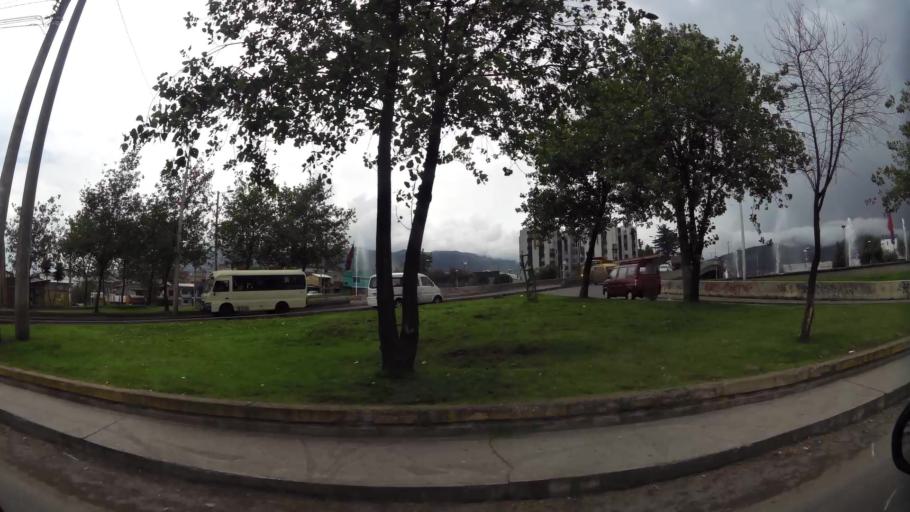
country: EC
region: Pichincha
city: Quito
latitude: -0.2899
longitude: -78.5374
